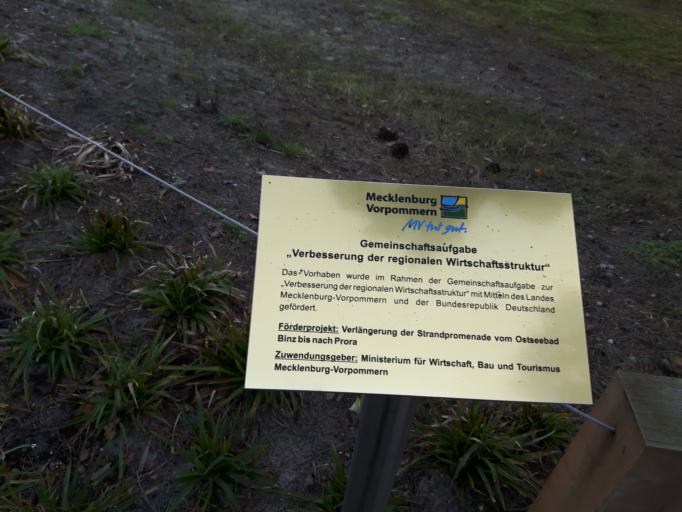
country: DE
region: Mecklenburg-Vorpommern
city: Ostseebad Binz
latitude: 54.4192
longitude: 13.5922
